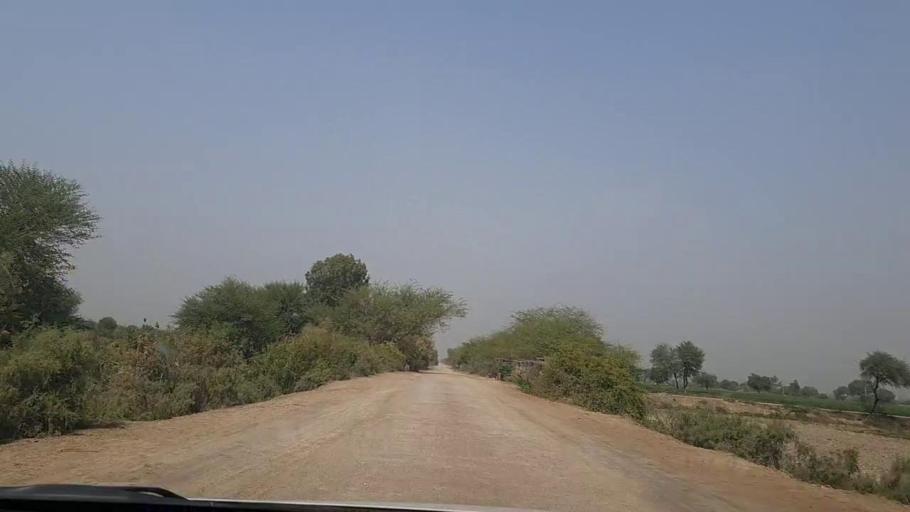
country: PK
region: Sindh
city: Mirpur Khas
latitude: 25.5849
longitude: 69.2010
